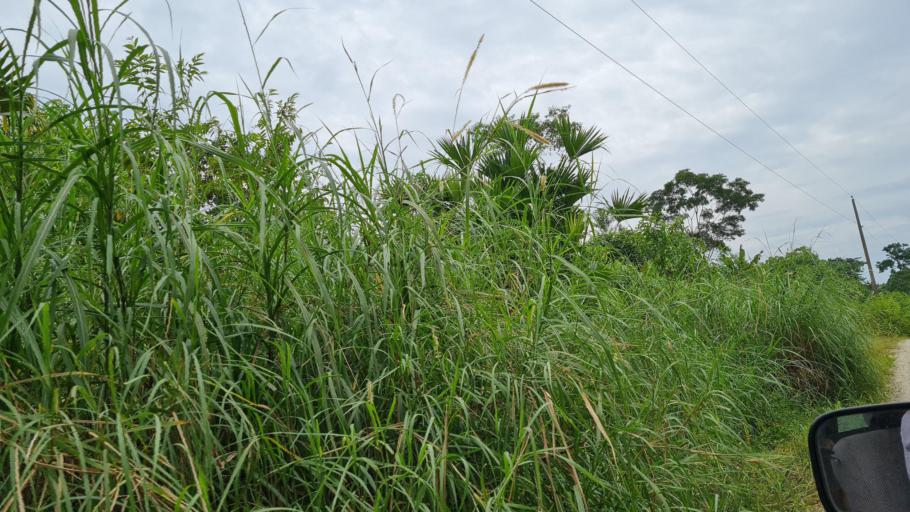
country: EC
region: Napo
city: Tena
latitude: -0.9964
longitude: -77.7531
